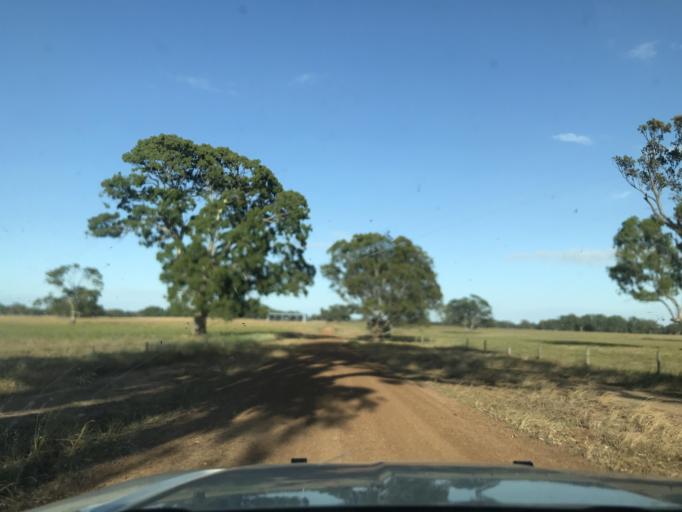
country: AU
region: South Australia
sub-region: Naracoorte and Lucindale
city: Naracoorte
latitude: -36.9555
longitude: 141.3661
